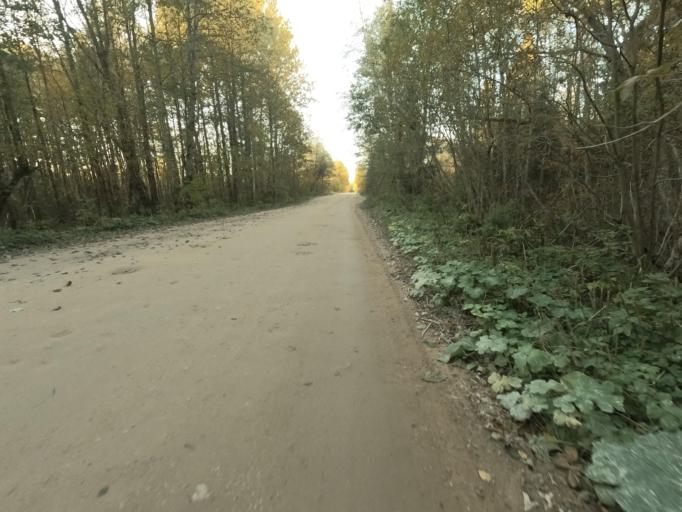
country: RU
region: Leningrad
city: Lyuban'
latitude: 59.0081
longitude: 31.0924
